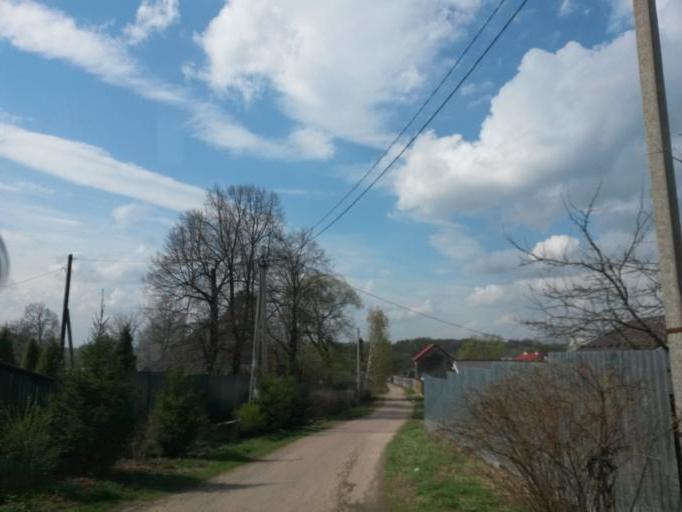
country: RU
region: Moskovskaya
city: Lyubuchany
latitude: 55.2556
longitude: 37.6047
